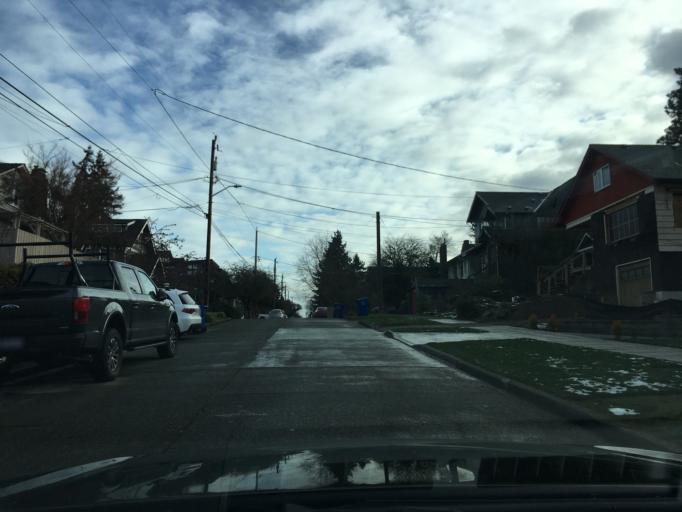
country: US
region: Washington
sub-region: King County
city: Seattle
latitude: 47.6716
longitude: -122.3316
